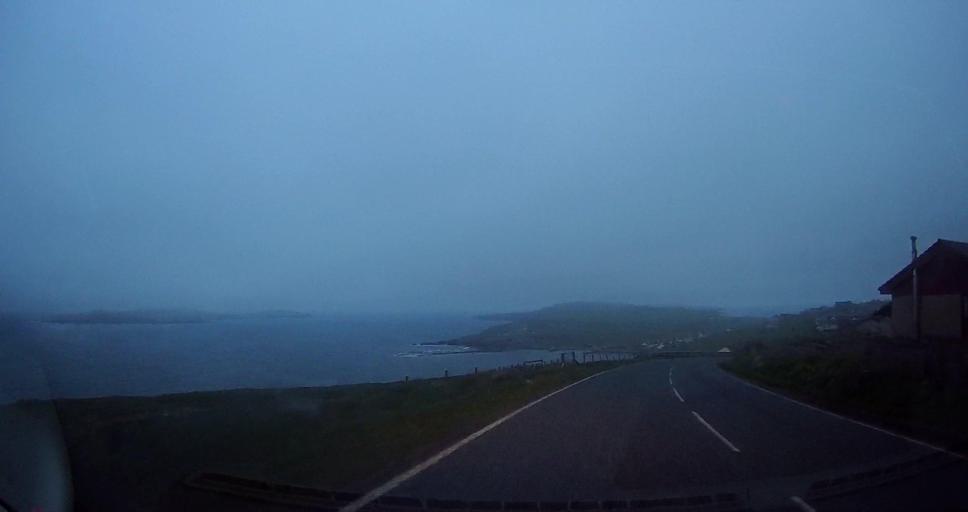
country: GB
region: Scotland
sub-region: Shetland Islands
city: Sandwick
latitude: 60.0136
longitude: -1.2267
